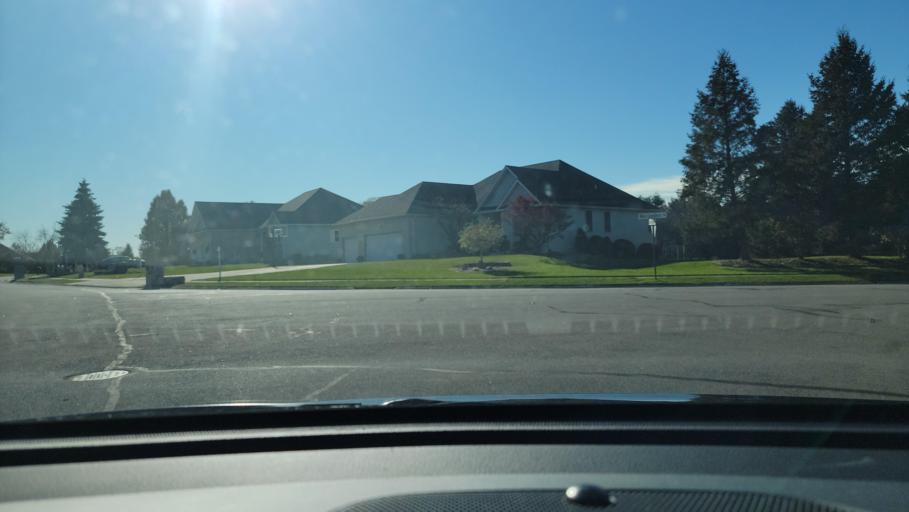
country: US
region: Indiana
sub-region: Porter County
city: Portage
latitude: 41.5918
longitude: -87.1489
